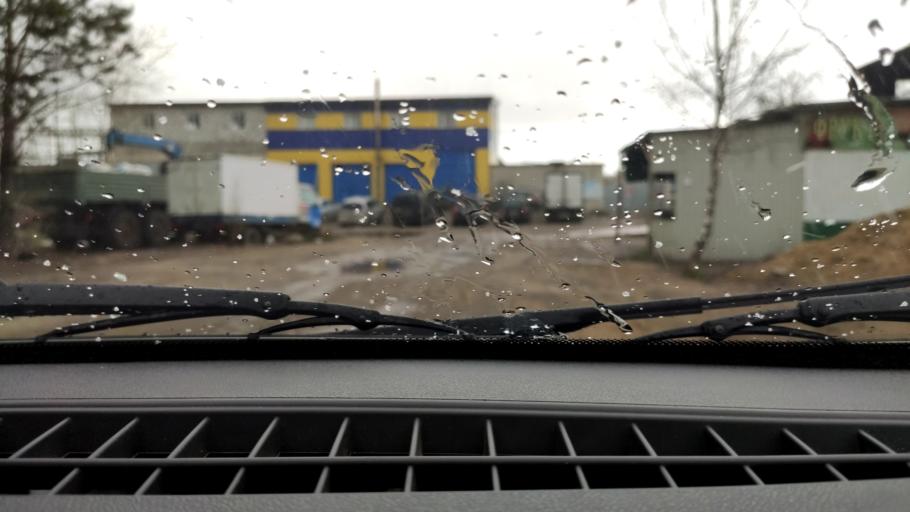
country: RU
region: Voronezj
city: Somovo
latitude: 51.7399
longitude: 39.3039
